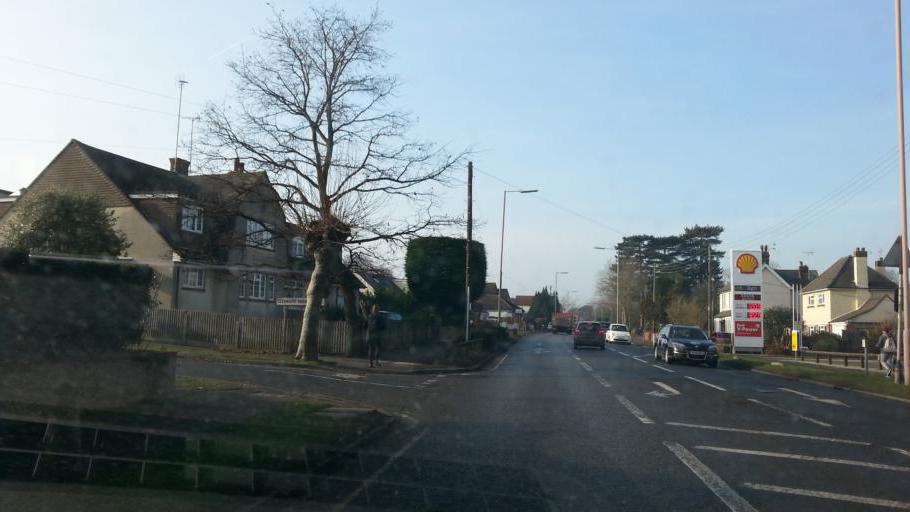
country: GB
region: England
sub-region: Essex
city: Hadleigh
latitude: 51.5603
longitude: 0.5918
